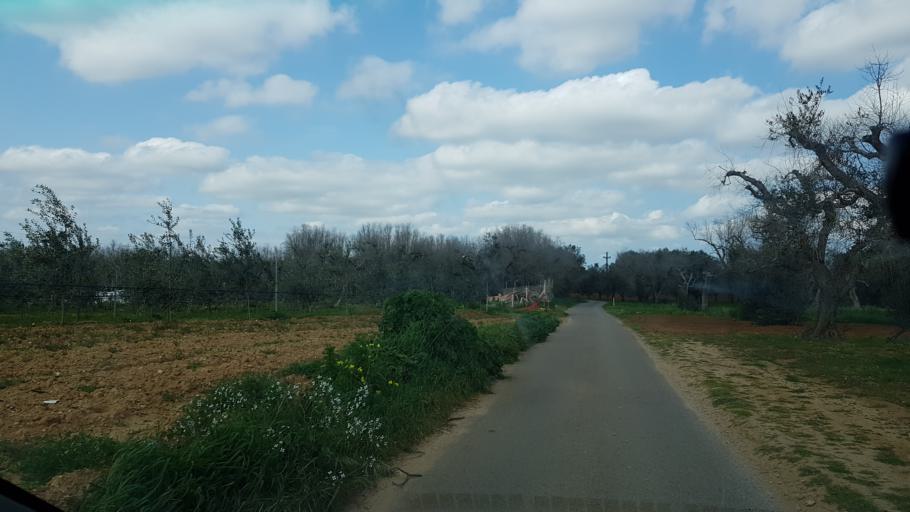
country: IT
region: Apulia
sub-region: Provincia di Brindisi
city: Torchiarolo
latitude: 40.4770
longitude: 18.0633
